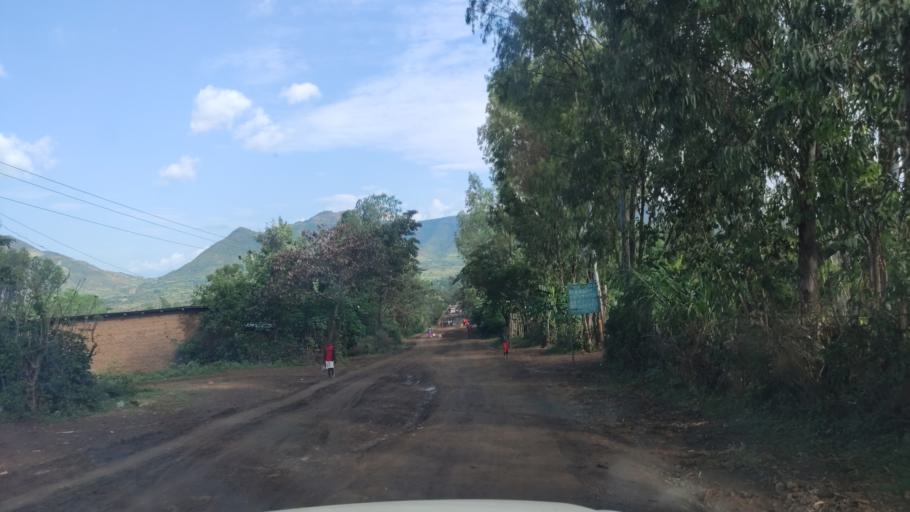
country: ET
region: Southern Nations, Nationalities, and People's Region
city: Felege Neway
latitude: 6.4264
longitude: 37.3063
